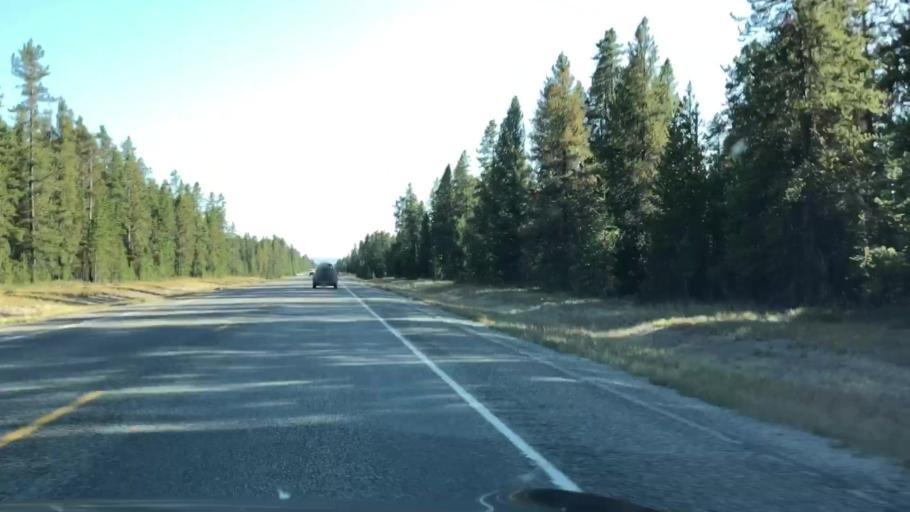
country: US
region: Montana
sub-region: Gallatin County
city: West Yellowstone
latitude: 44.7563
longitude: -111.1133
